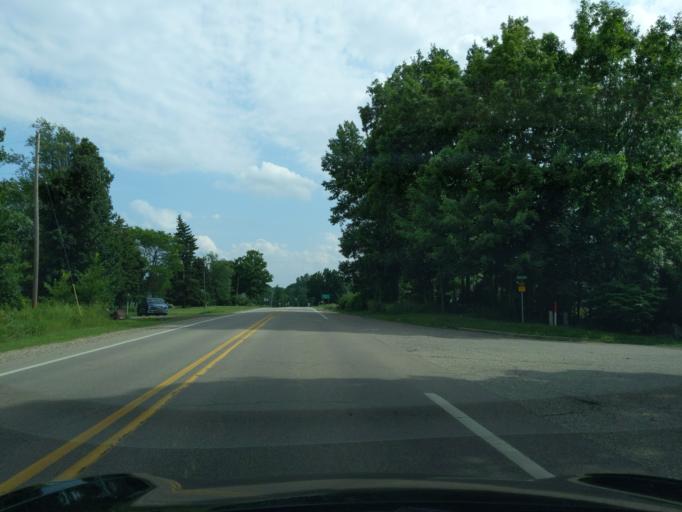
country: US
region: Michigan
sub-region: Eaton County
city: Eaton Rapids
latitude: 42.4259
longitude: -84.6497
